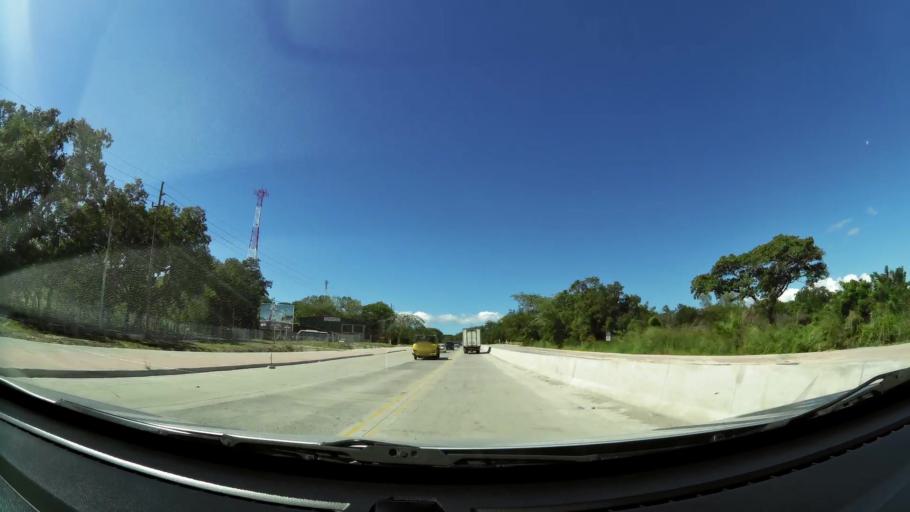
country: CR
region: Guanacaste
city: Liberia
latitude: 10.5686
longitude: -85.3924
